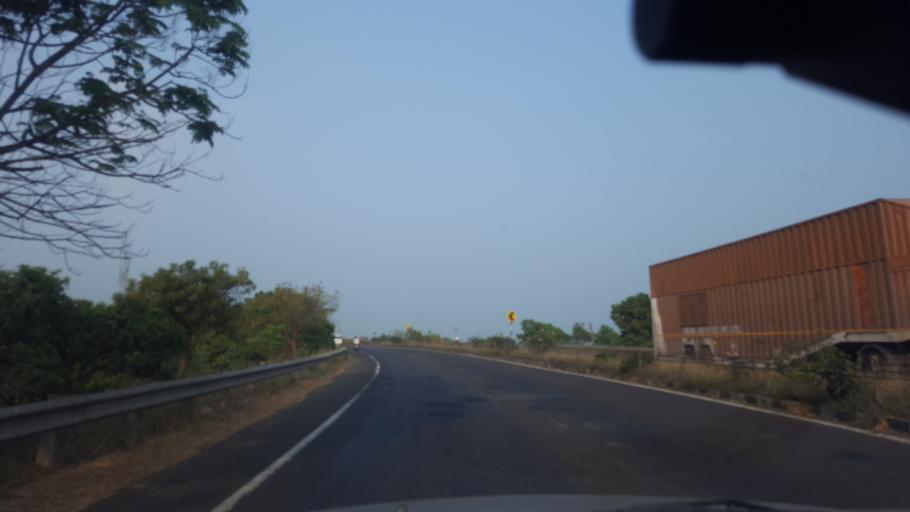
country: IN
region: Andhra Pradesh
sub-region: West Godavari
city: Tadepallegudem
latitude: 16.8259
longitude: 81.4654
